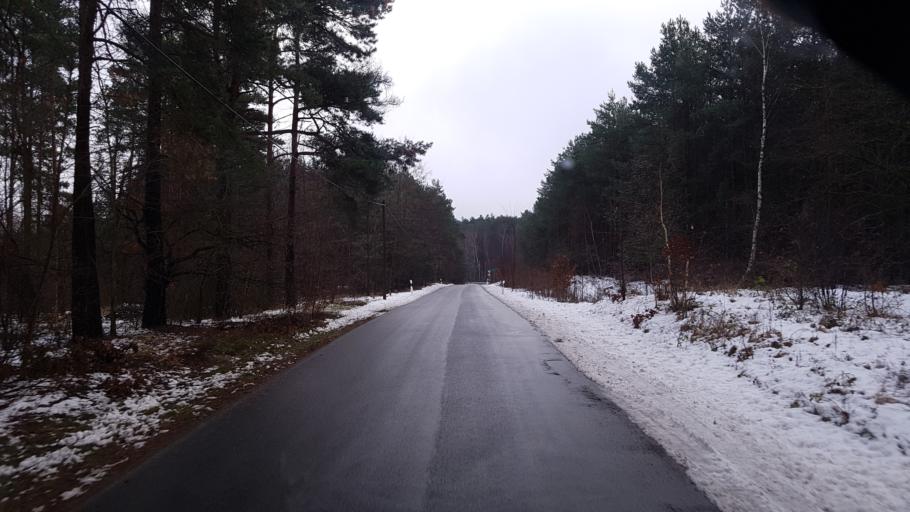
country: DE
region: Brandenburg
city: Straupitz
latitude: 51.9737
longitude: 14.2002
